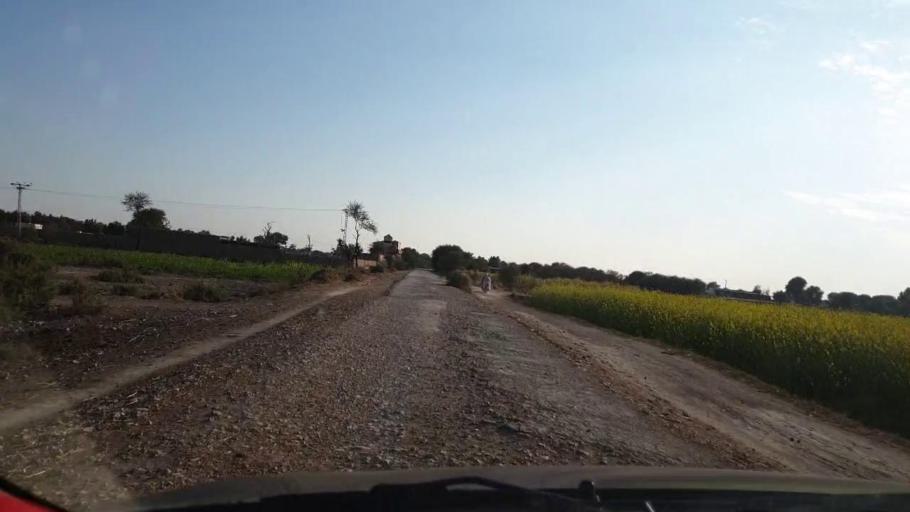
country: PK
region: Sindh
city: Jhol
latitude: 25.9524
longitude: 68.8615
